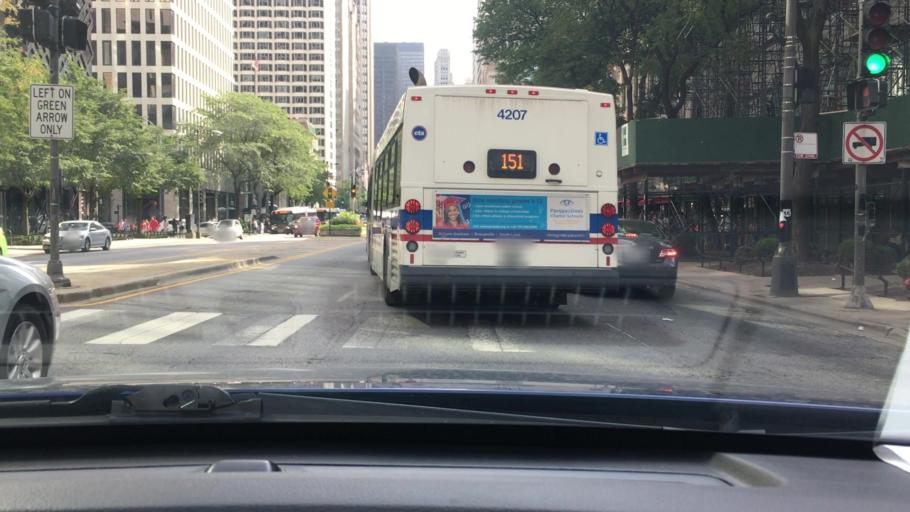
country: US
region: Illinois
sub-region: Cook County
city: Chicago
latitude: 41.8941
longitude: -87.6243
